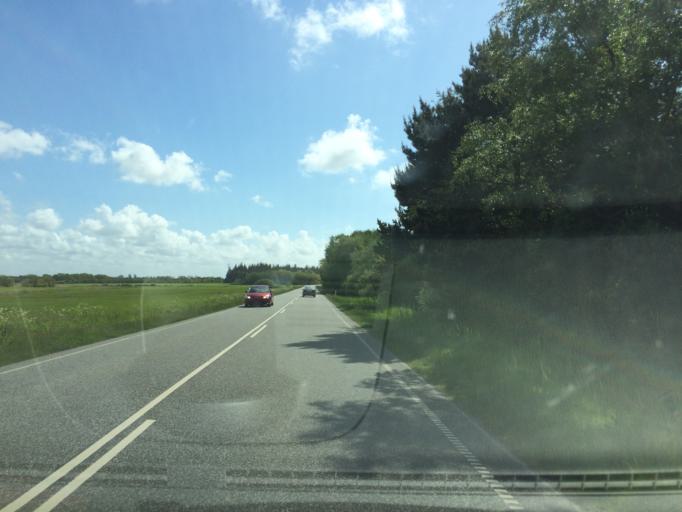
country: DK
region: Central Jutland
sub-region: Holstebro Kommune
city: Ulfborg
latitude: 56.2945
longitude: 8.1879
